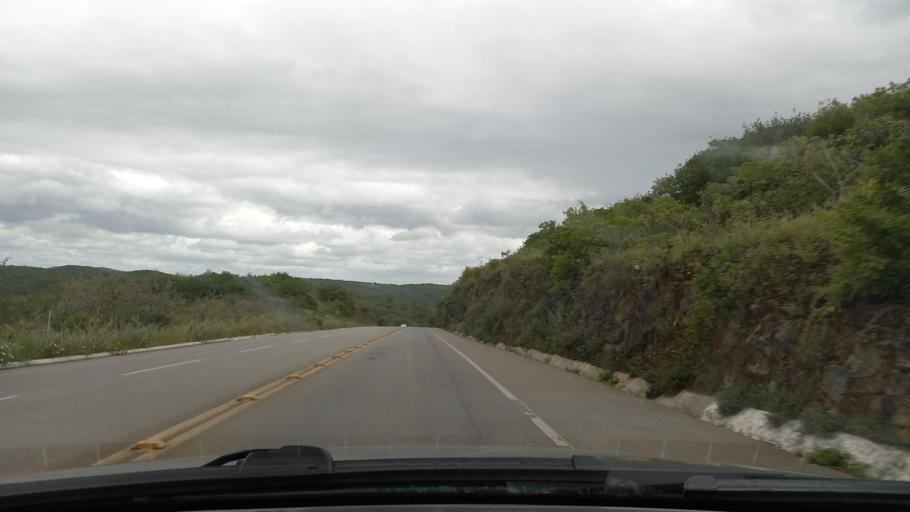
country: BR
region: Sergipe
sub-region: Caninde De Sao Francisco
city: Caninde de Sao Francisco
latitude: -9.6504
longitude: -37.7929
